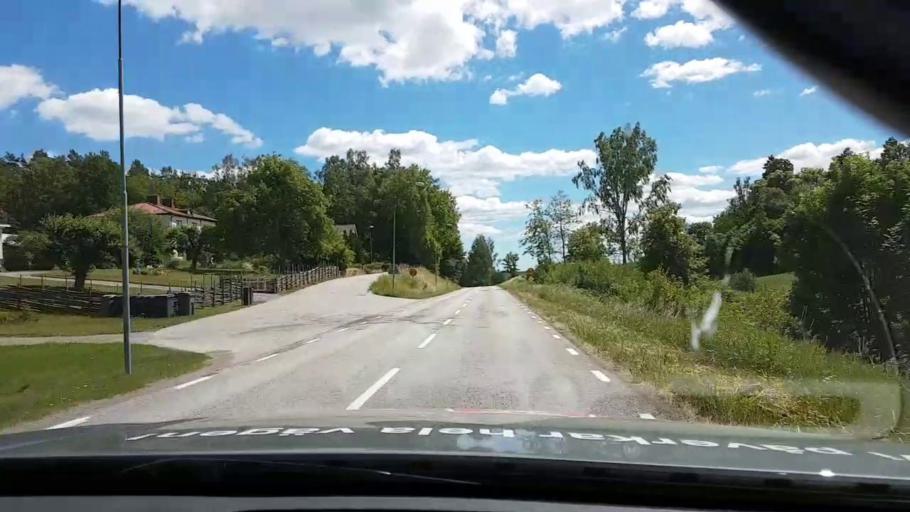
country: SE
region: Kalmar
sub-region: Vasterviks Kommun
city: Overum
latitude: 58.0791
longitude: 16.3552
